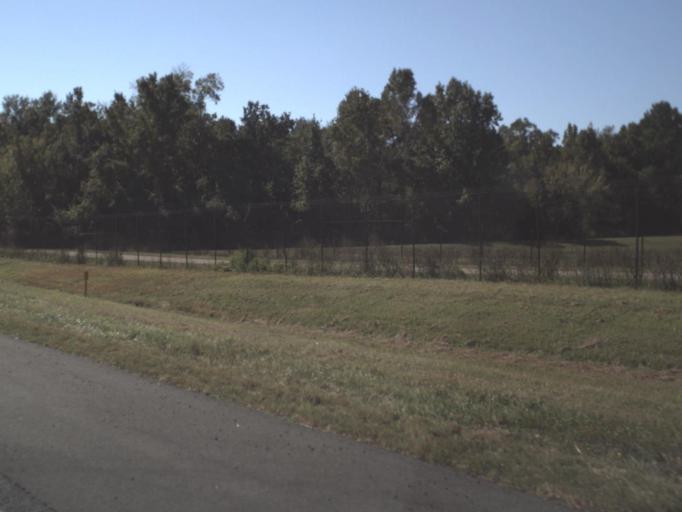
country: US
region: Florida
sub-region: Hernando County
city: Brookridge
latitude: 28.6389
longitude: -82.4896
